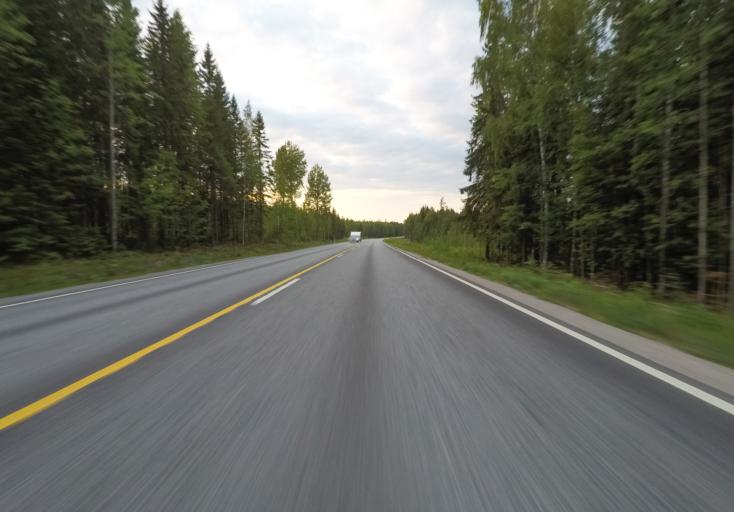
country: FI
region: Central Finland
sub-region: Jyvaeskylae
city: Toivakka
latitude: 62.2170
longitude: 26.2058
